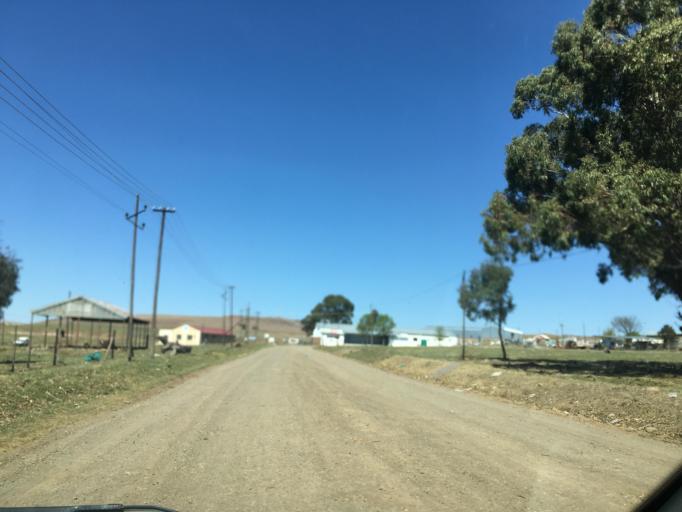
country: ZA
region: Eastern Cape
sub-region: Chris Hani District Municipality
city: Elliot
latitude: -31.3379
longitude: 27.8403
